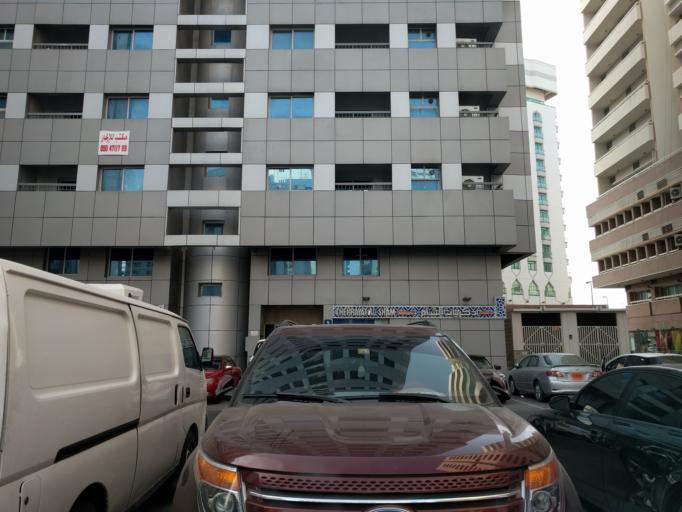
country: AE
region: Abu Dhabi
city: Abu Dhabi
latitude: 24.5026
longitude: 54.3740
